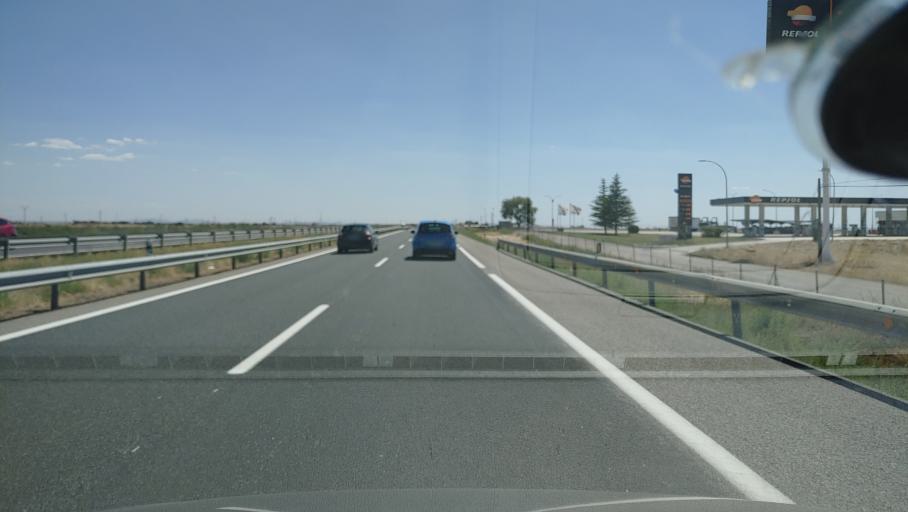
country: ES
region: Castille-La Mancha
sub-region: Provincia de Ciudad Real
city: Villarta de San Juan
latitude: 39.1817
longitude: -3.3988
